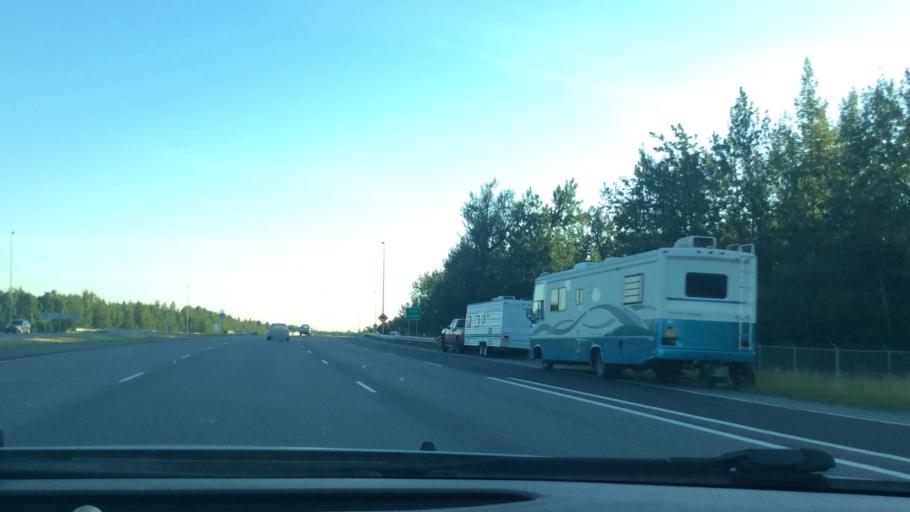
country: US
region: Alaska
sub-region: Anchorage Municipality
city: Elmendorf Air Force Base
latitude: 61.2395
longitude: -149.6915
